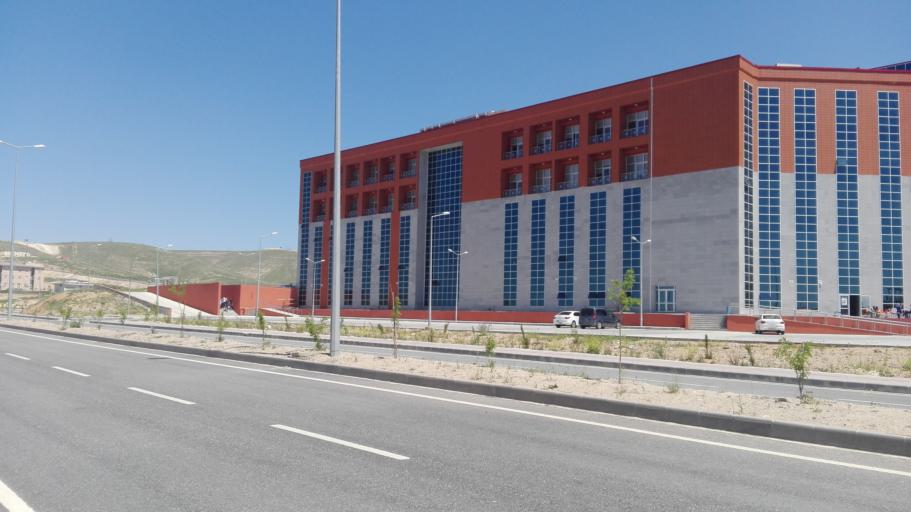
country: TR
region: Batman
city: Oymatas
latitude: 37.7890
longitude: 41.0615
